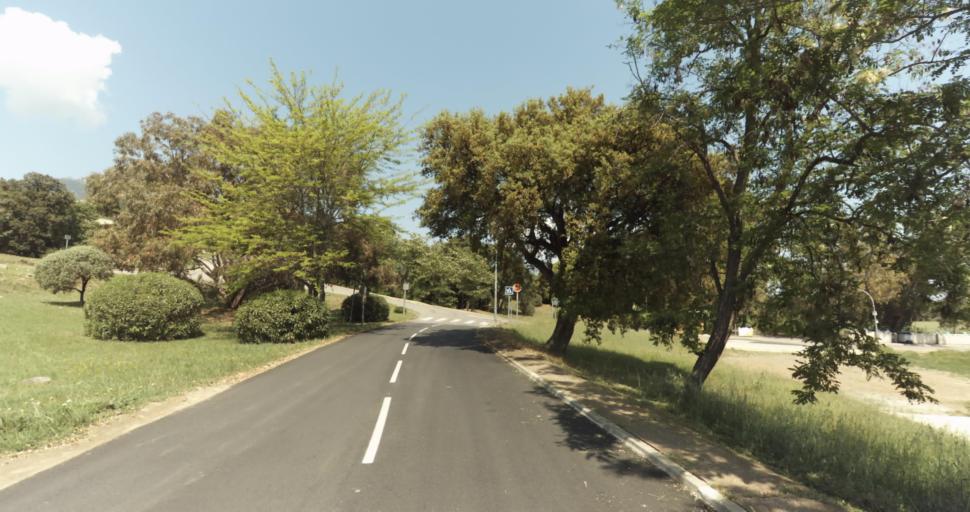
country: FR
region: Corsica
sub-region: Departement de la Haute-Corse
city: Biguglia
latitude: 42.6053
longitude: 9.4337
